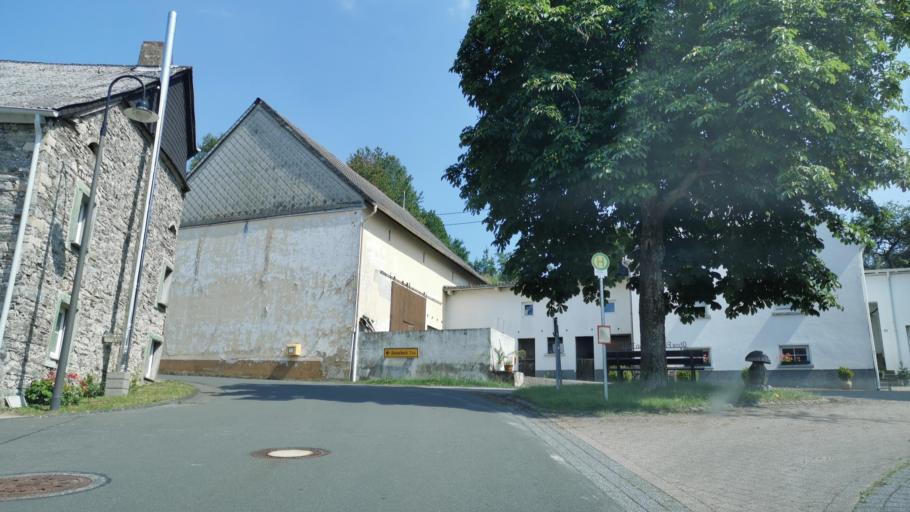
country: DE
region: Rheinland-Pfalz
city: Rorodt
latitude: 49.7687
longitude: 7.0498
